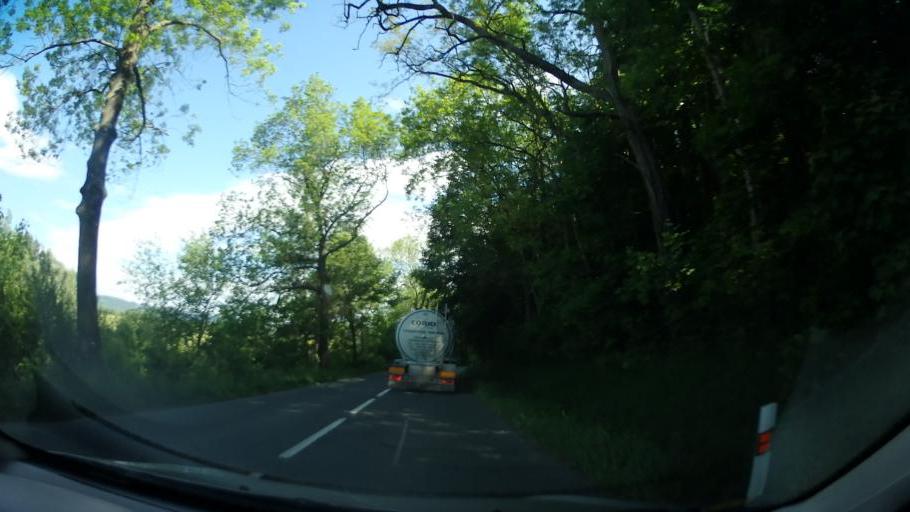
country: CZ
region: Pardubicky
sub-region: Okres Svitavy
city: Moravska Trebova
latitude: 49.7242
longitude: 16.6407
